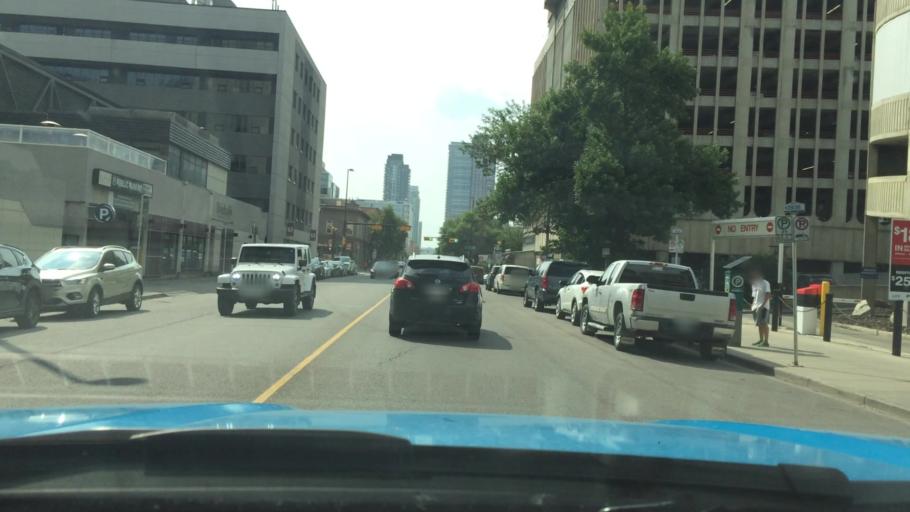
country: CA
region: Alberta
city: Calgary
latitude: 51.0434
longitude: -114.0639
